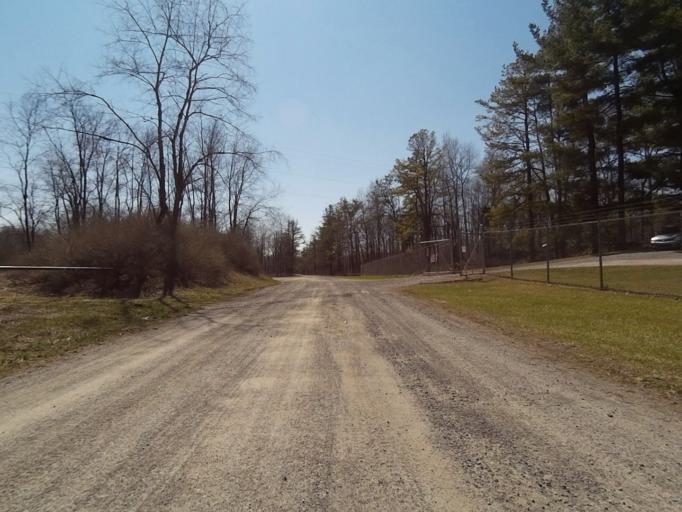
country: US
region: Pennsylvania
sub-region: Centre County
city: Stormstown
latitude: 40.7717
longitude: -77.9657
